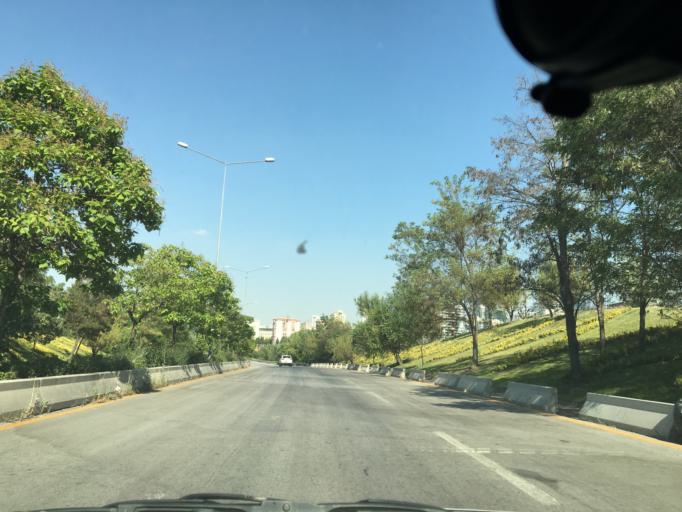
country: TR
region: Ankara
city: Ankara
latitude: 39.9174
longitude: 32.7928
